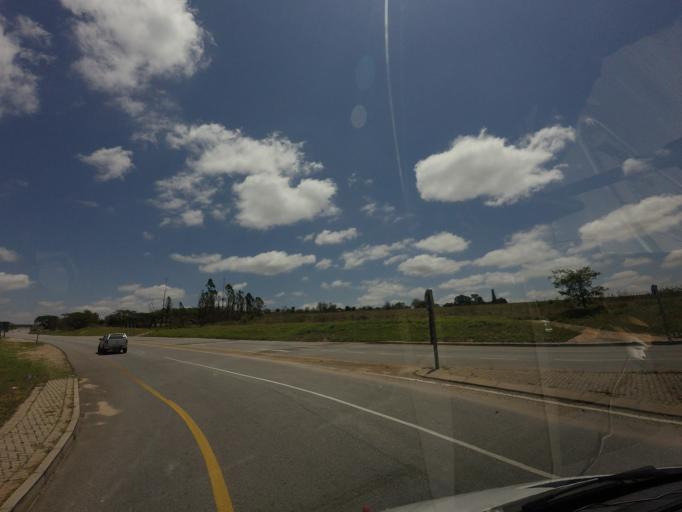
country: ZA
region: Mpumalanga
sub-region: Ehlanzeni District
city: Nelspruit
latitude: -25.4422
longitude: 30.9537
